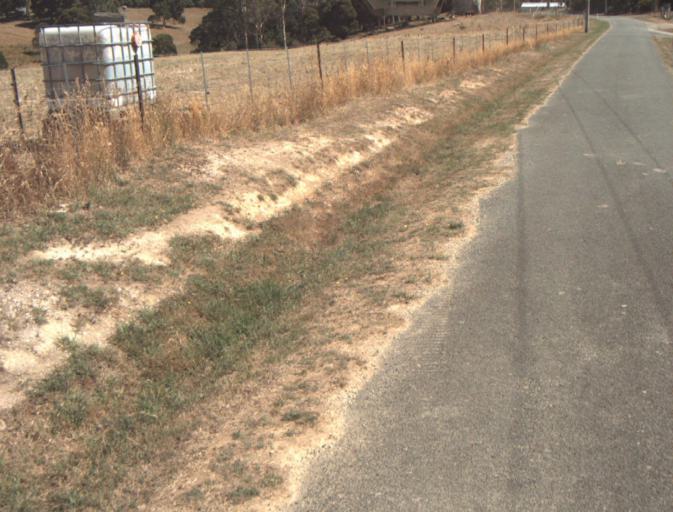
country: AU
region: Tasmania
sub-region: Launceston
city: Mayfield
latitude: -41.2353
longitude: 147.2560
